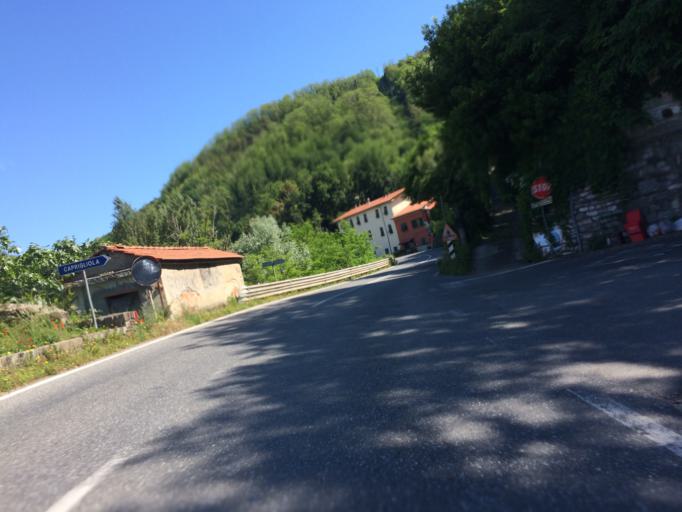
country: IT
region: Tuscany
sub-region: Provincia di Massa-Carrara
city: Albiano Magra
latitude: 44.1757
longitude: 9.9285
